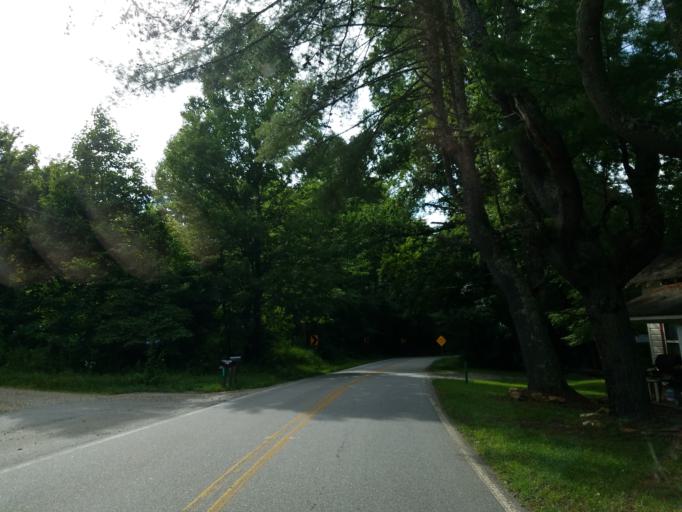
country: US
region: Georgia
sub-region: Lumpkin County
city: Dahlonega
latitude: 34.7022
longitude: -84.0539
